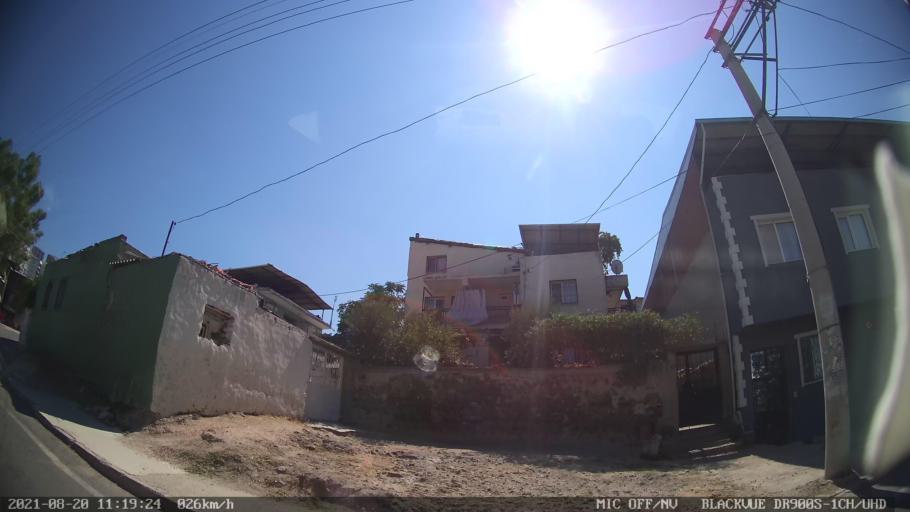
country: TR
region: Izmir
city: Karsiyaka
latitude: 38.5005
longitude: 27.0696
